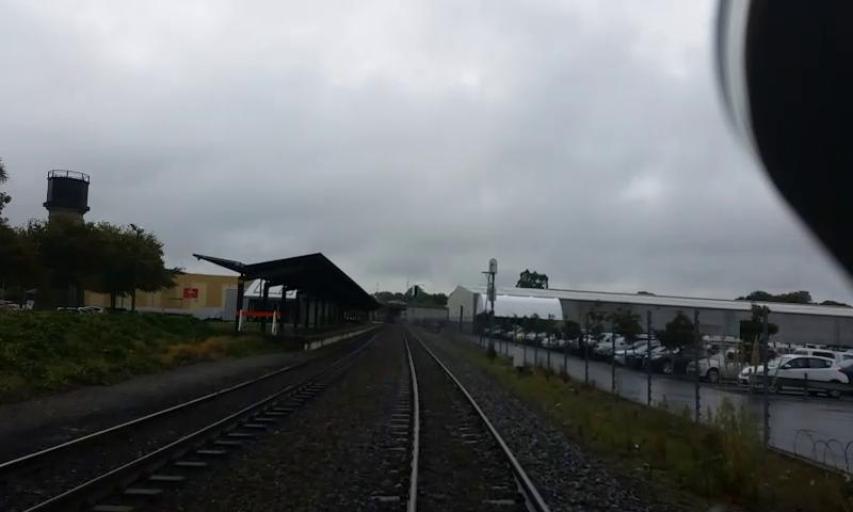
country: NZ
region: Canterbury
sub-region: Christchurch City
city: Christchurch
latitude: -43.5402
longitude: 172.6079
